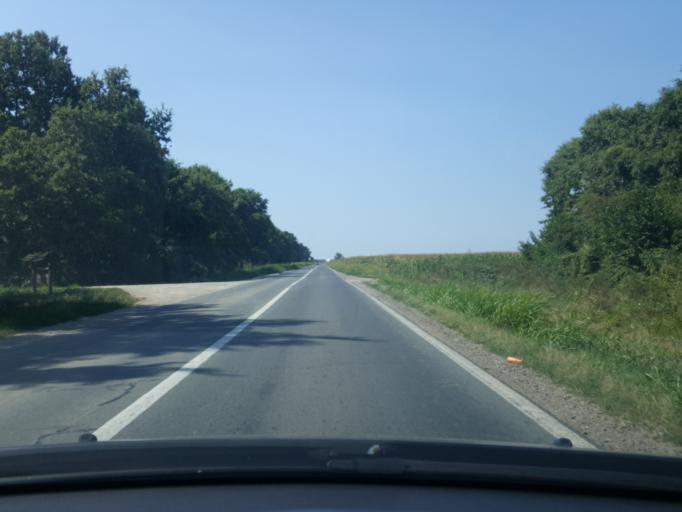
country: RS
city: Platicevo
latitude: 44.8377
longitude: 19.7713
